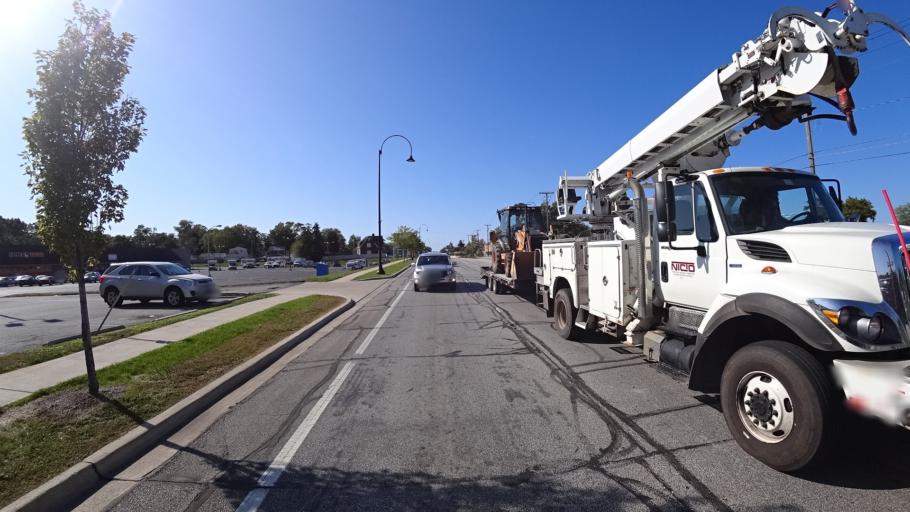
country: US
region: Indiana
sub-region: LaPorte County
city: Trail Creek
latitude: 41.7087
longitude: -86.8699
